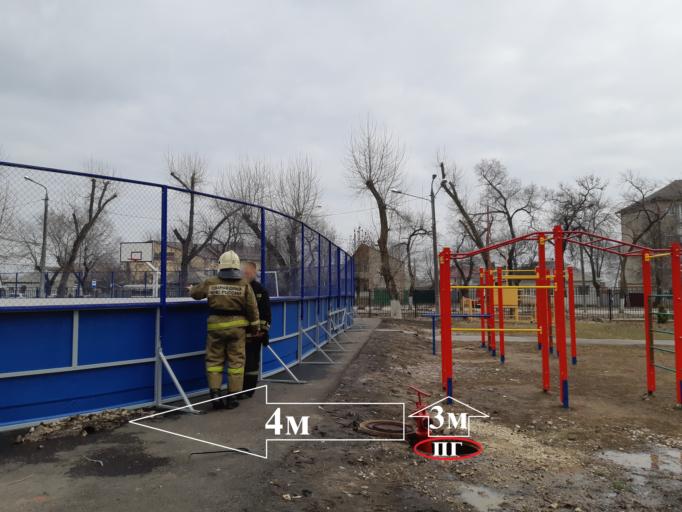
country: RU
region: Voronezj
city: Voronezh
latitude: 51.6462
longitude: 39.1824
